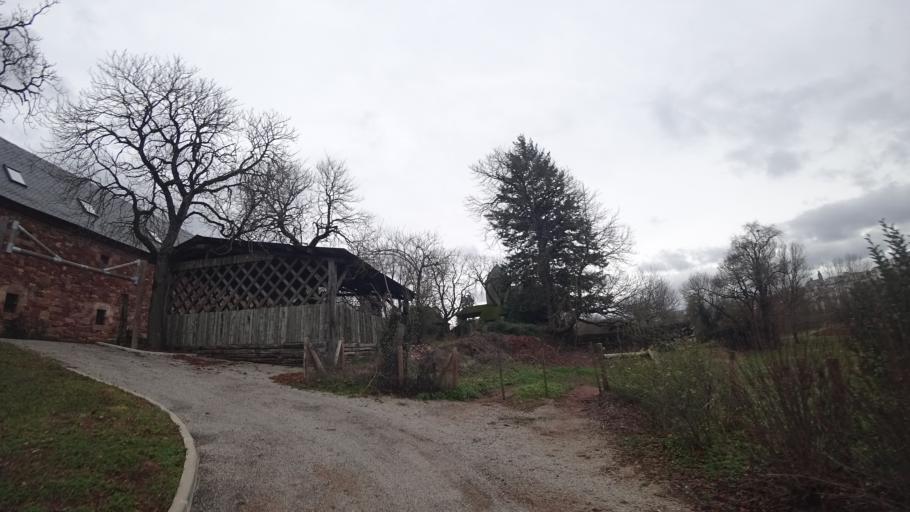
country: FR
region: Midi-Pyrenees
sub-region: Departement de l'Aveyron
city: Rodez
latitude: 44.3657
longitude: 2.5655
